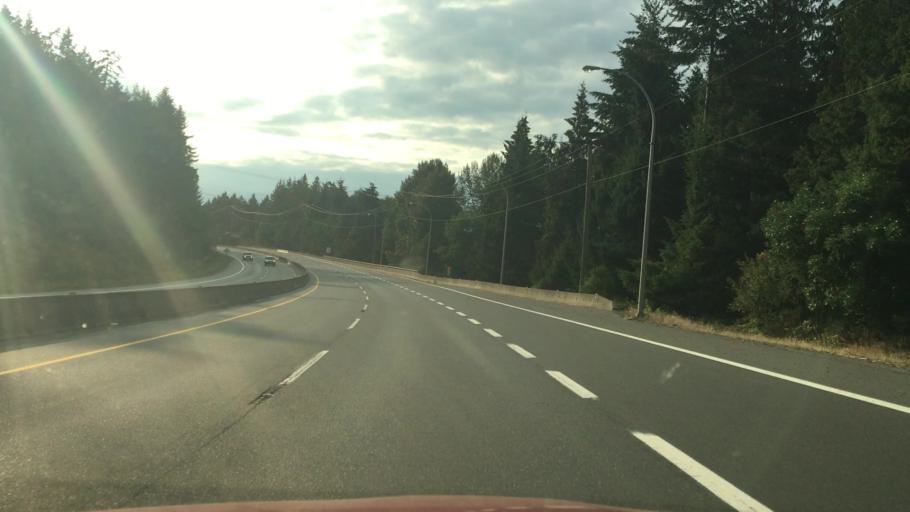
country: CA
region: British Columbia
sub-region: Regional District of Nanaimo
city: Parksville
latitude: 49.3015
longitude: -124.2586
